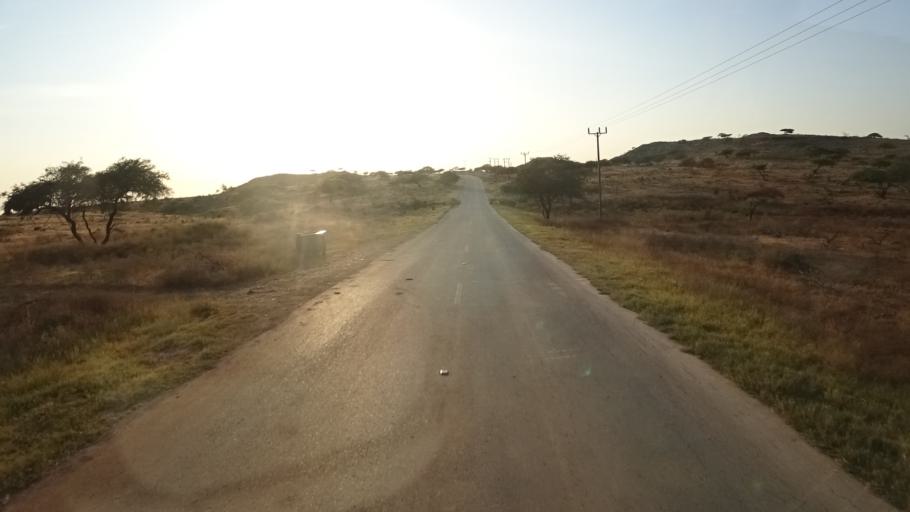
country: OM
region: Zufar
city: Salalah
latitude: 17.1481
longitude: 54.6069
